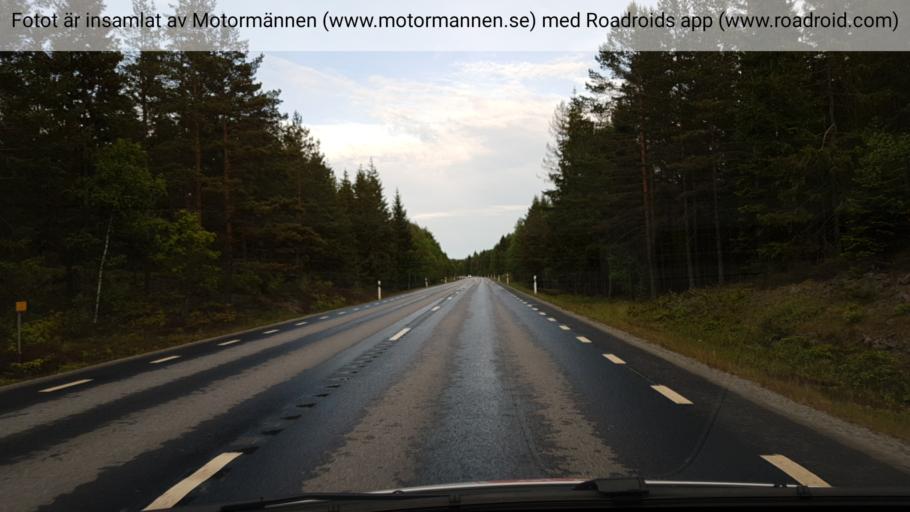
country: SE
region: Kalmar
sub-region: Vasterviks Kommun
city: Ankarsrum
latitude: 57.7224
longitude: 16.3670
